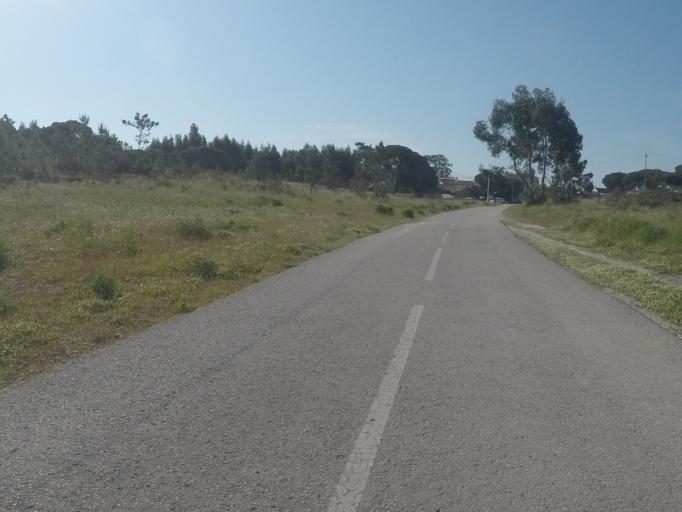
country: PT
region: Setubal
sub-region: Sesimbra
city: Sesimbra
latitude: 38.4823
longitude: -9.1618
